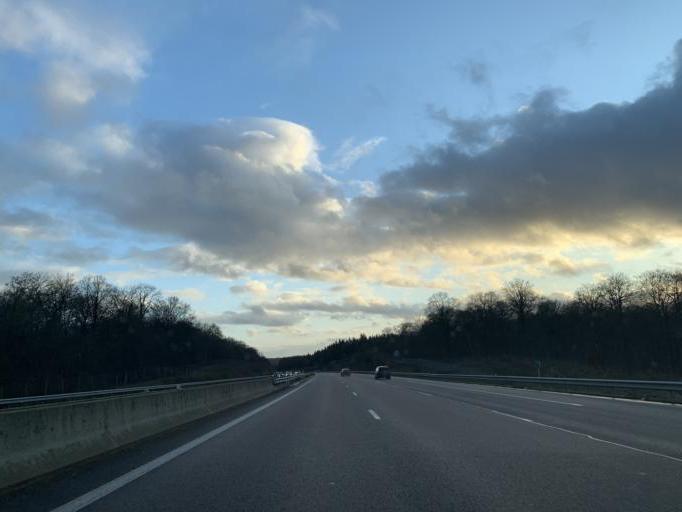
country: FR
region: Bourgogne
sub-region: Departement de la Cote-d'Or
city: Selongey
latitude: 47.6691
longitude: 5.1747
